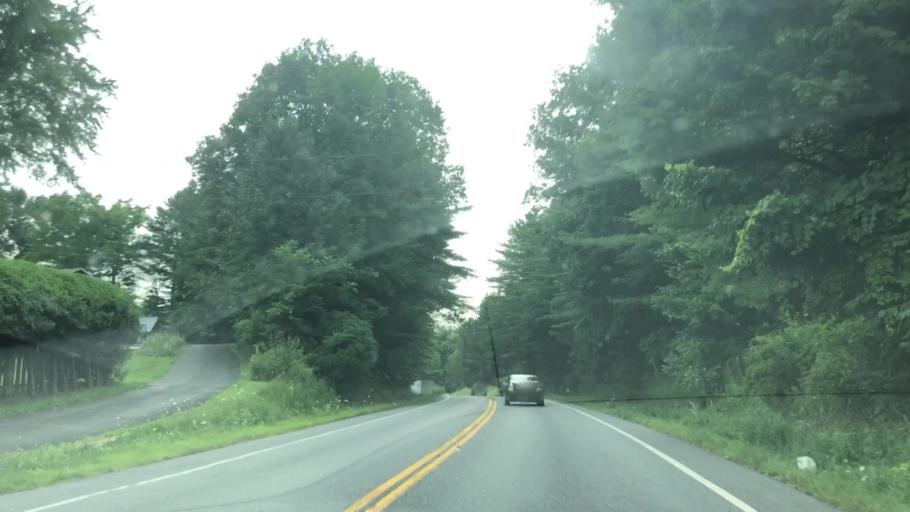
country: US
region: New York
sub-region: Warren County
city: Queensbury
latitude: 43.4080
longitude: -73.5714
